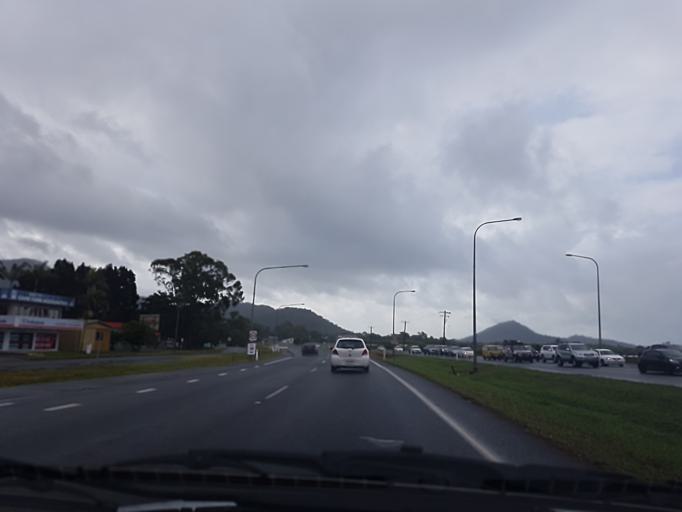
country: AU
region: Queensland
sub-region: Cairns
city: Yorkeys Knob
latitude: -16.8311
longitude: 145.6932
